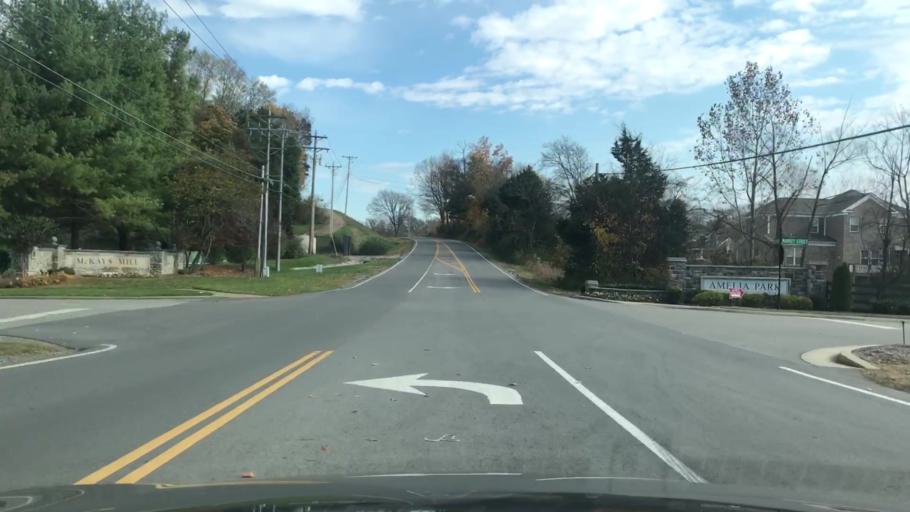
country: US
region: Tennessee
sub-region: Williamson County
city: Franklin
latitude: 35.9206
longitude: -86.7802
